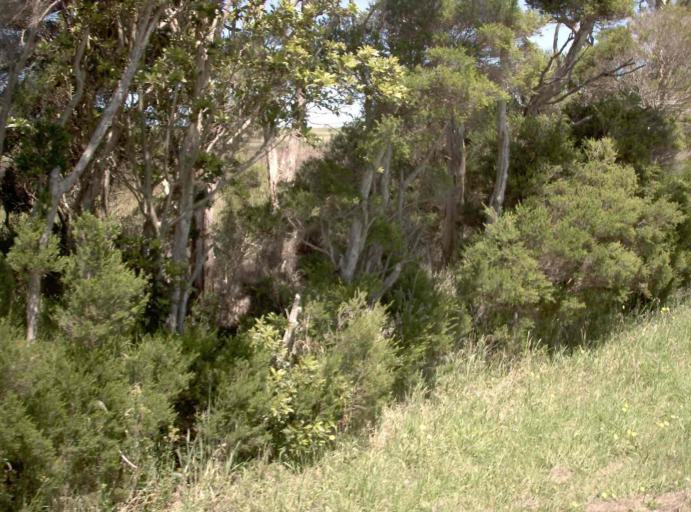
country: AU
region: Victoria
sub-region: Bass Coast
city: North Wonthaggi
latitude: -38.7486
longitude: 146.0750
